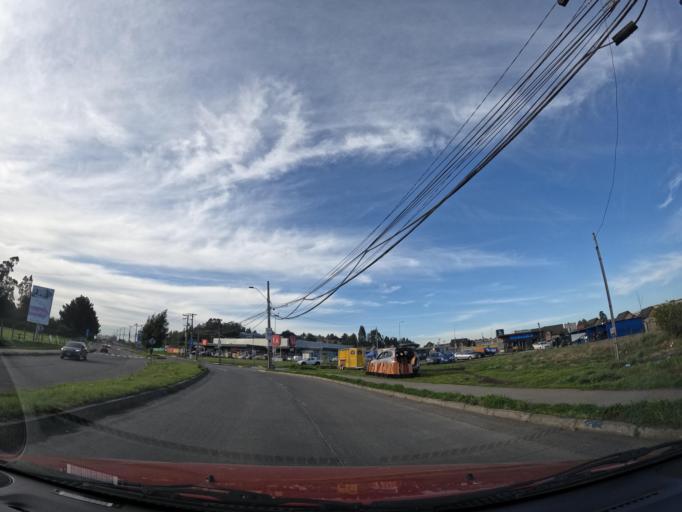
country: CL
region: Biobio
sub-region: Provincia de Concepcion
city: Concepcion
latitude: -36.7883
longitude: -73.0547
